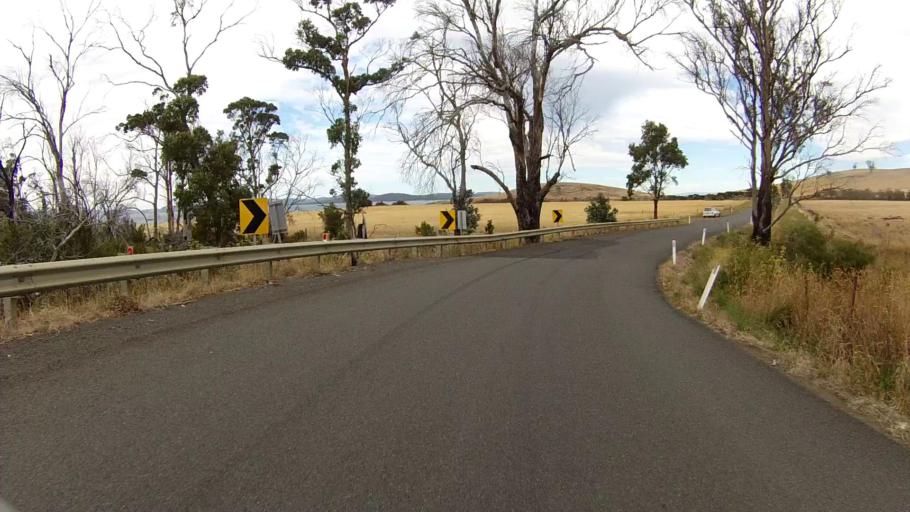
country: AU
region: Tasmania
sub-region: Sorell
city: Sorell
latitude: -42.8941
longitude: 147.7786
